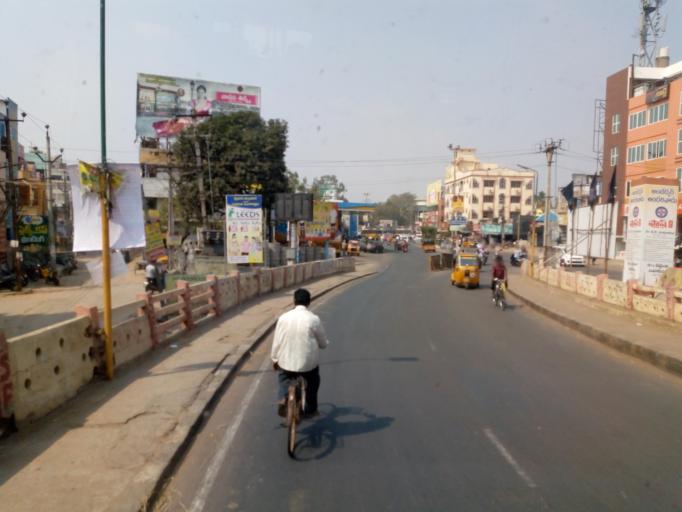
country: IN
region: Andhra Pradesh
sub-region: West Godavari
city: Eluru
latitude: 16.7099
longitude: 81.0957
